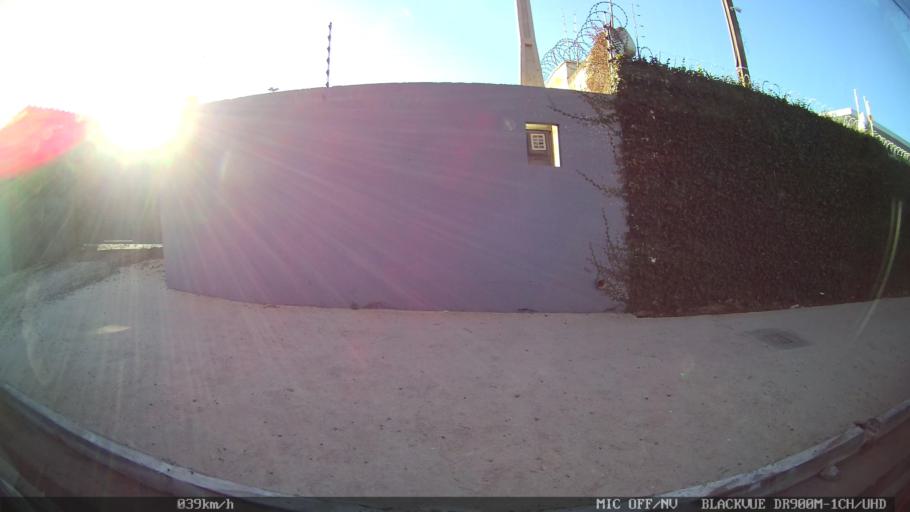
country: BR
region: Sao Paulo
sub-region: Sao Jose Do Rio Preto
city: Sao Jose do Rio Preto
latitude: -20.8084
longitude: -49.3710
